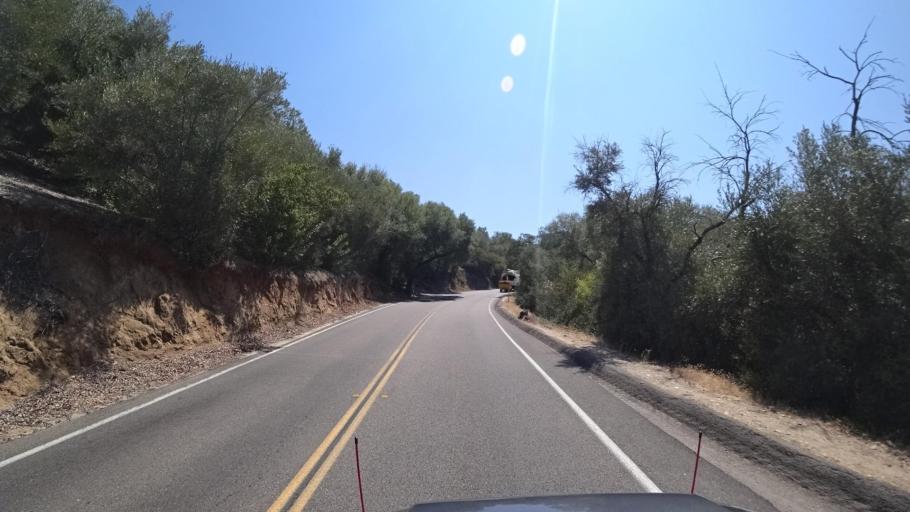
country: US
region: California
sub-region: San Diego County
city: Fallbrook
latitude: 33.3963
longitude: -117.2519
